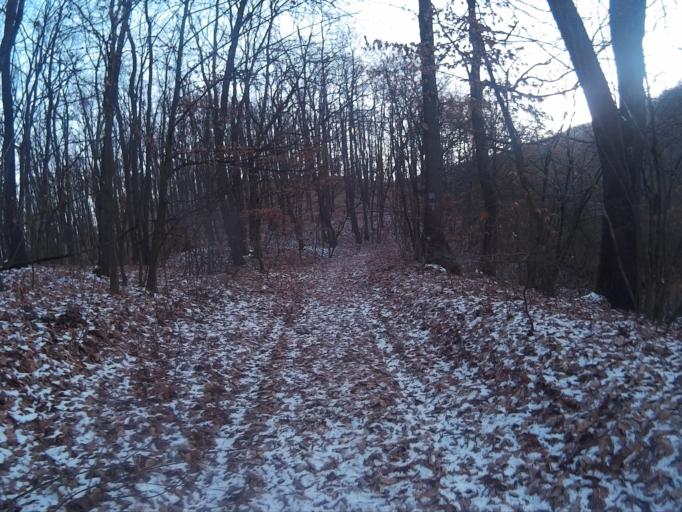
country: HU
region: Borsod-Abauj-Zemplen
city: Putnok
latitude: 48.3377
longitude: 20.4247
